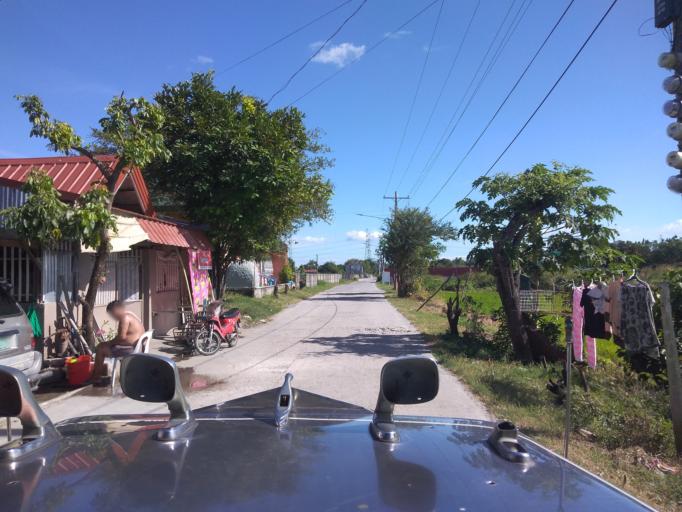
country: PH
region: Central Luzon
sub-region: Province of Pampanga
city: Bacolor
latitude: 15.0093
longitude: 120.6451
